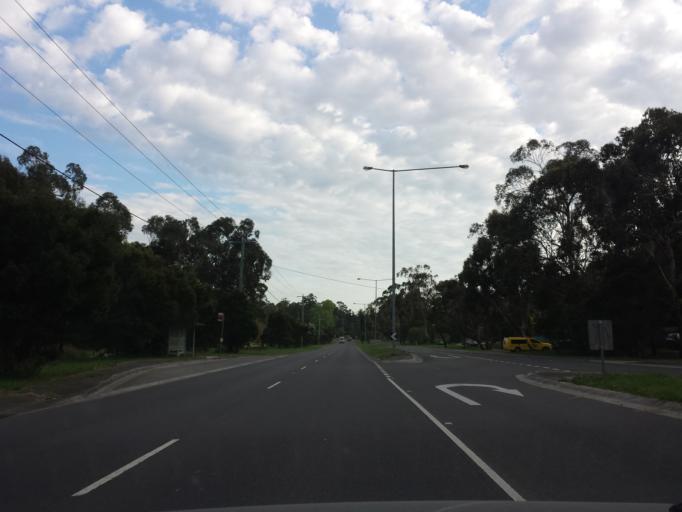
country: AU
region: Victoria
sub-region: Yarra Ranges
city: Mount Evelyn
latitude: -37.7888
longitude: 145.3613
